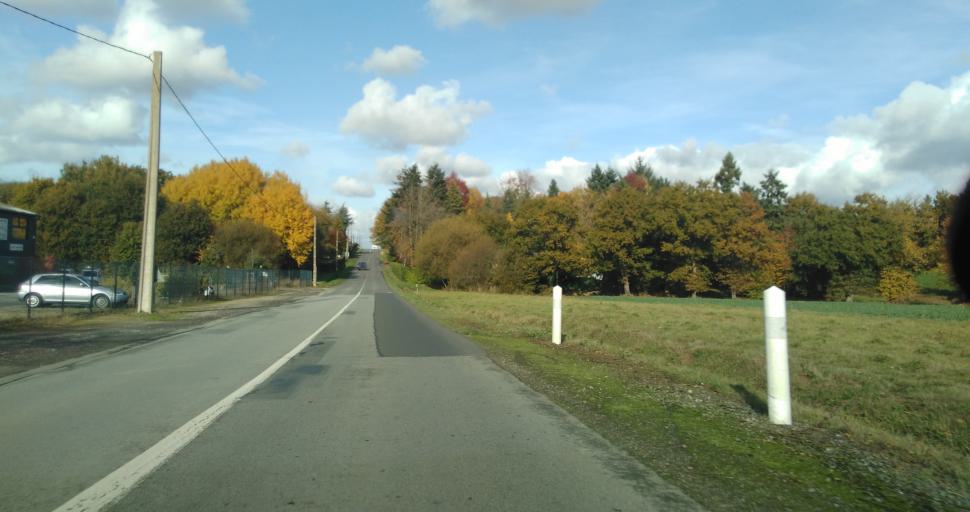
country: FR
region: Brittany
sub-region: Departement d'Ille-et-Vilaine
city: Montauban-de-Bretagne
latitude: 48.1822
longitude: -2.0490
